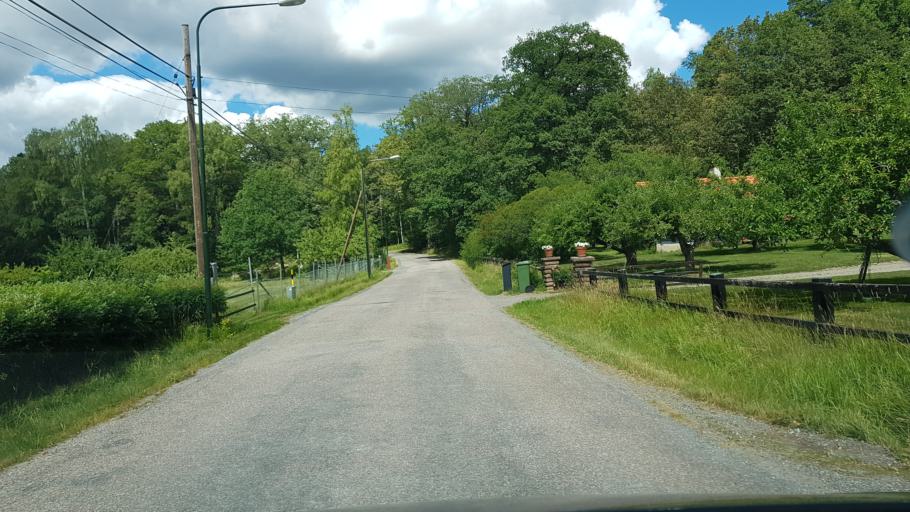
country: SE
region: Stockholm
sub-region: Upplands-Bro Kommun
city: Kungsaengen
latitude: 59.4943
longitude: 17.8057
